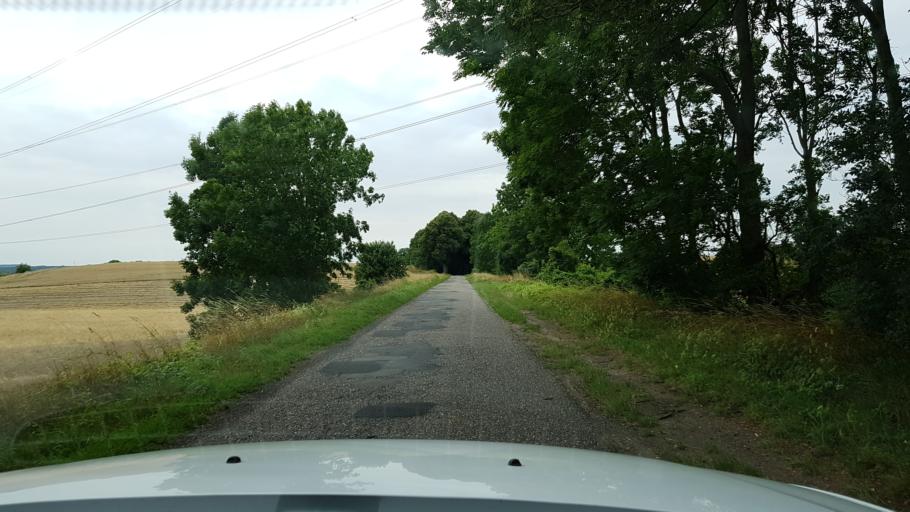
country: DE
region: Brandenburg
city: Gartz
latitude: 53.1692
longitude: 14.4244
